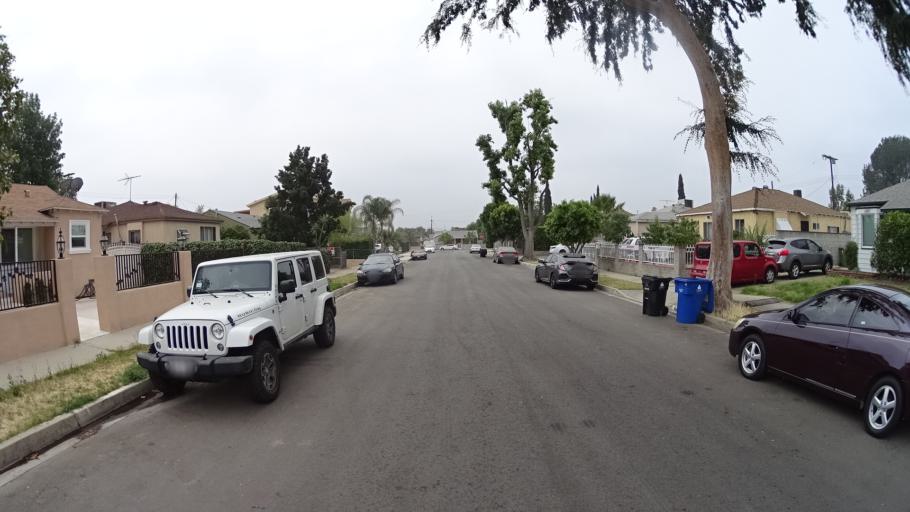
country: US
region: California
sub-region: Los Angeles County
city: North Hollywood
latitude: 34.1884
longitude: -118.4081
